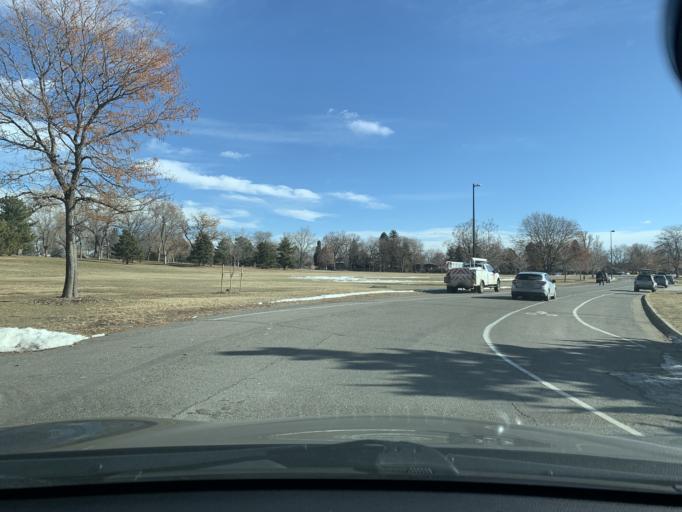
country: US
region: Colorado
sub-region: Jefferson County
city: Edgewater
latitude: 39.7531
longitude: -105.0462
